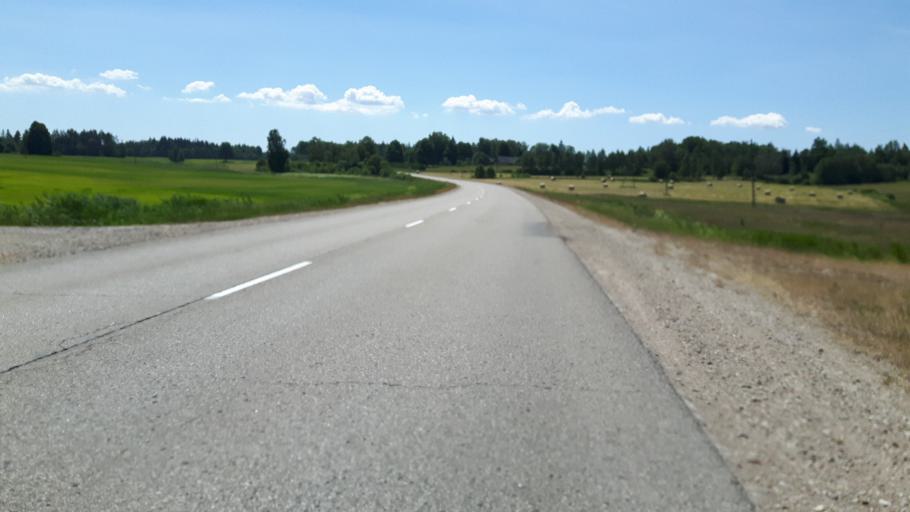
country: LV
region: Kuldigas Rajons
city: Kuldiga
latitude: 56.9205
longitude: 21.9066
